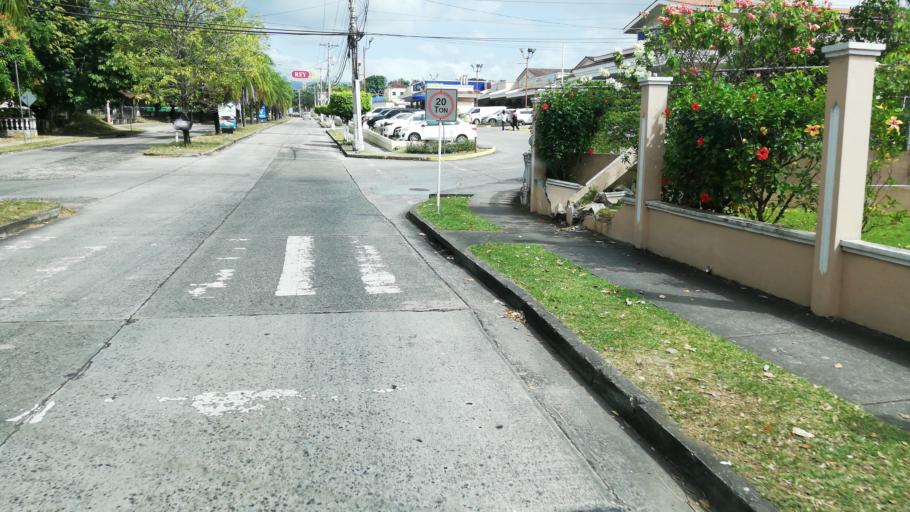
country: PA
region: Panama
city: San Miguelito
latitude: 9.0668
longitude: -79.4531
